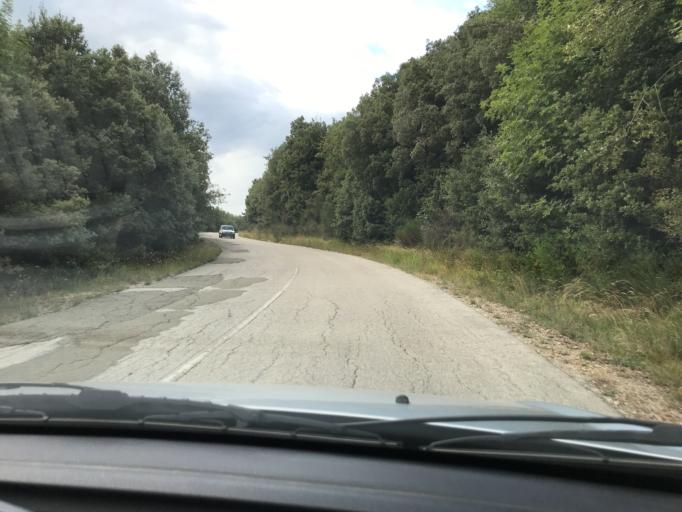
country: IT
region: Umbria
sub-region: Provincia di Terni
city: Montecchio
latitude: 42.6830
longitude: 12.3005
